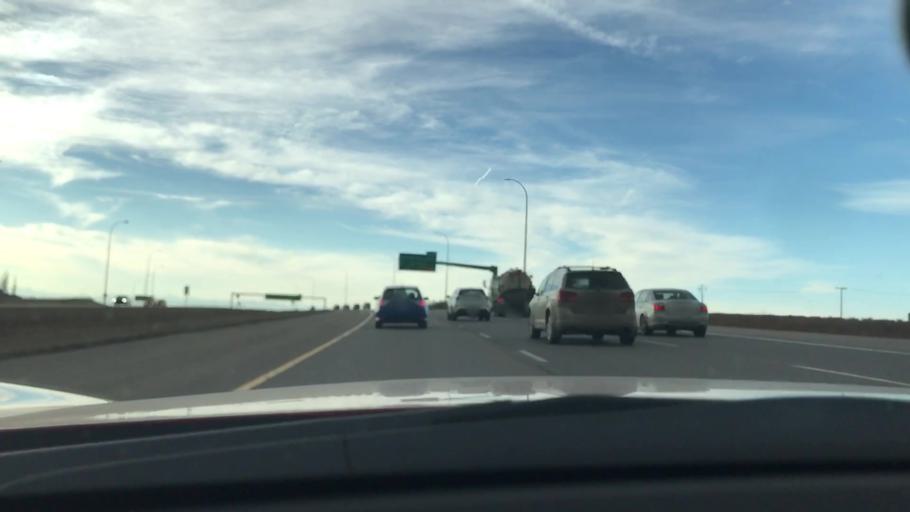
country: CA
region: Alberta
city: Calgary
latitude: 51.1502
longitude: -114.1930
